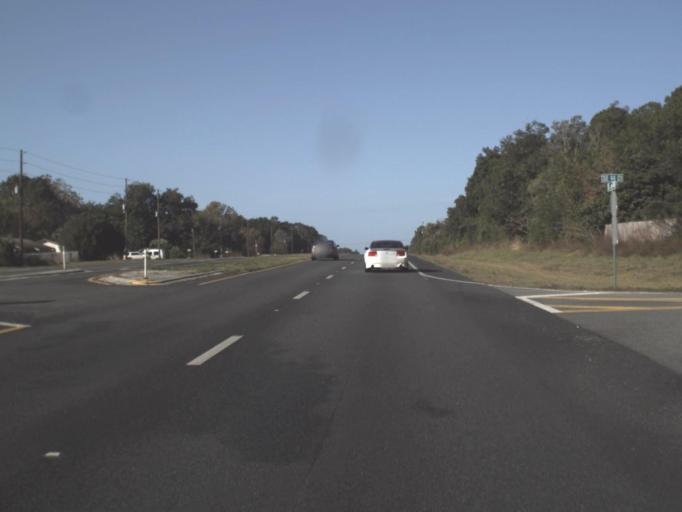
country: US
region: Florida
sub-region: Marion County
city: Belleview
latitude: 29.0261
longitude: -82.0742
